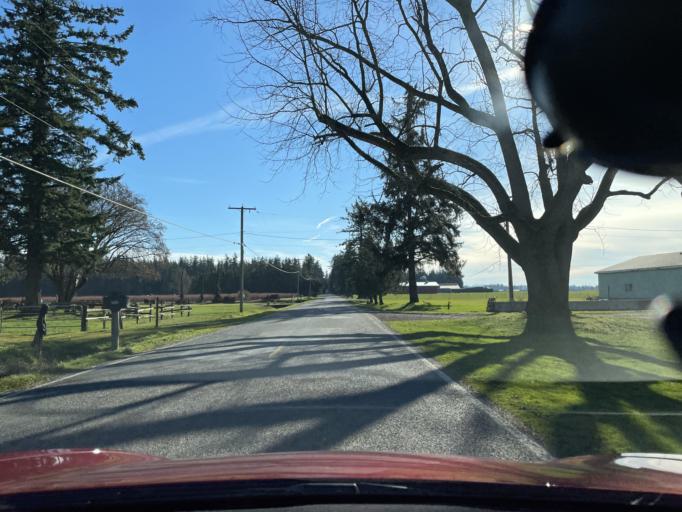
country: US
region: Washington
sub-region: Whatcom County
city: Lynden
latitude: 48.9766
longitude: -122.5130
